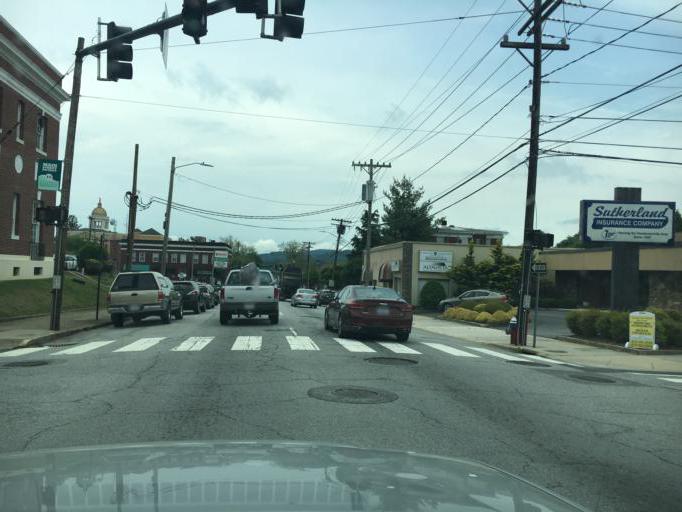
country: US
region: North Carolina
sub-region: Henderson County
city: Hendersonville
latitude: 35.3168
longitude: -82.4615
